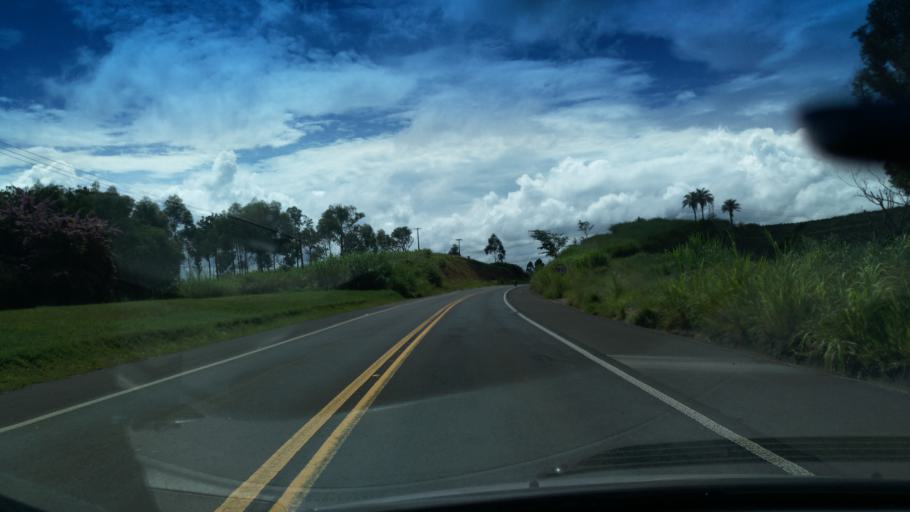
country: BR
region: Sao Paulo
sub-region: Santo Antonio Do Jardim
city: Espirito Santo do Pinhal
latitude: -22.1414
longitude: -46.7117
